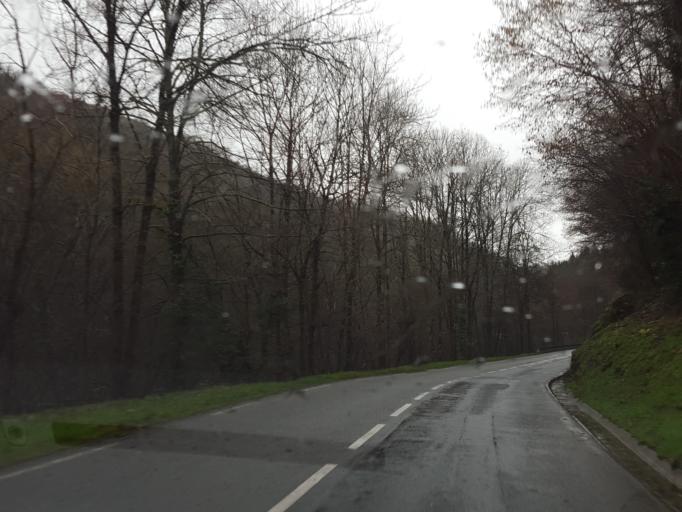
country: FR
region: Midi-Pyrenees
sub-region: Departement de l'Ariege
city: Saint-Girons
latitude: 42.9120
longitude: 1.2072
